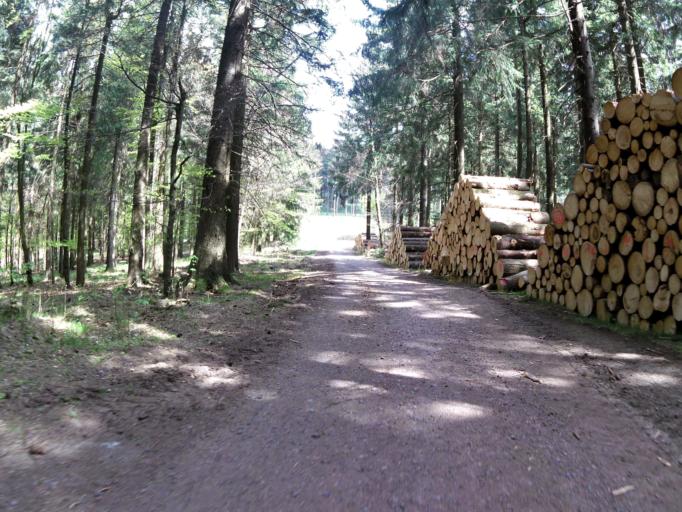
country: DE
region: Thuringia
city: Brotterode
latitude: 50.8441
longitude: 10.4368
